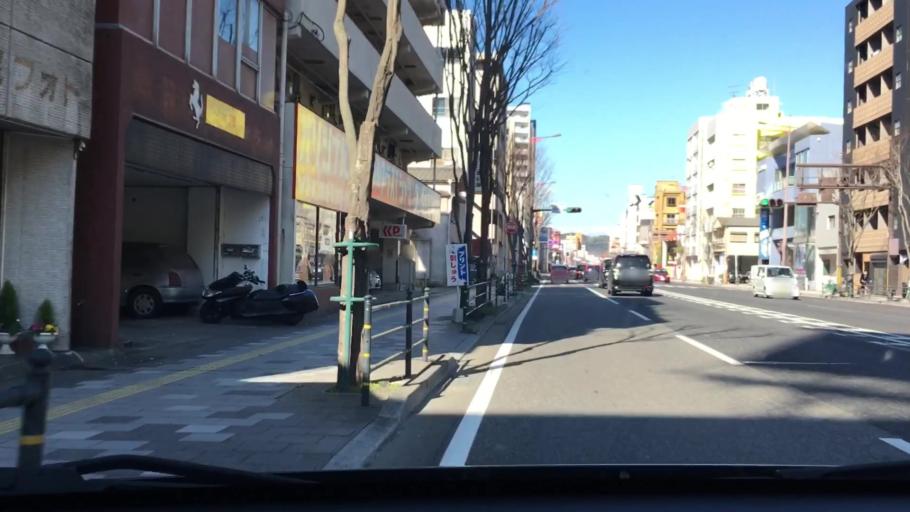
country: JP
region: Kagoshima
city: Kagoshima-shi
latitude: 31.5977
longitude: 130.5409
